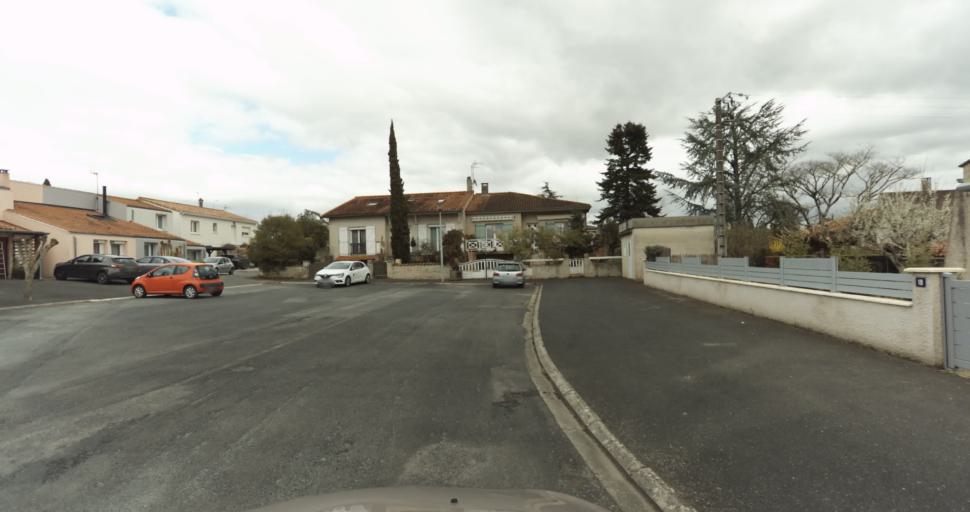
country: FR
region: Midi-Pyrenees
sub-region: Departement du Tarn
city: Puygouzon
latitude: 43.8927
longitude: 2.1786
